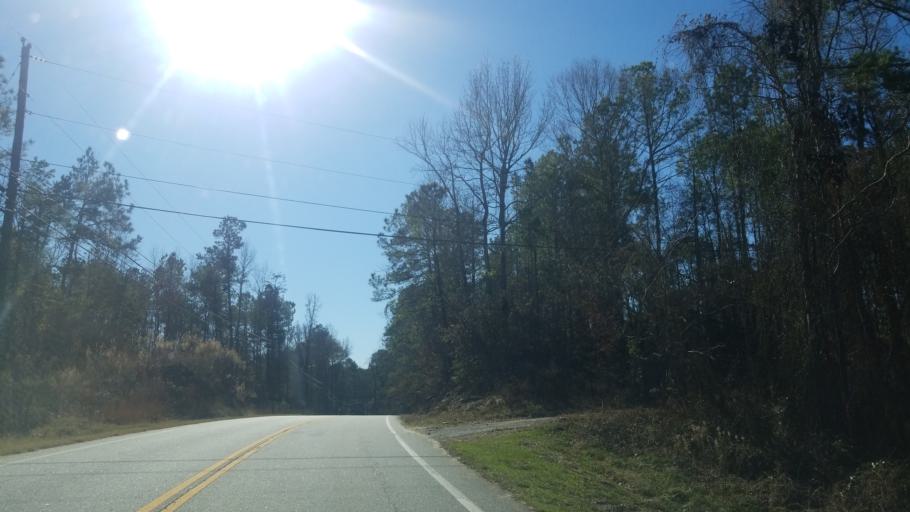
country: US
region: Alabama
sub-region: Lee County
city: Smiths Station
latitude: 32.5791
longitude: -85.0168
